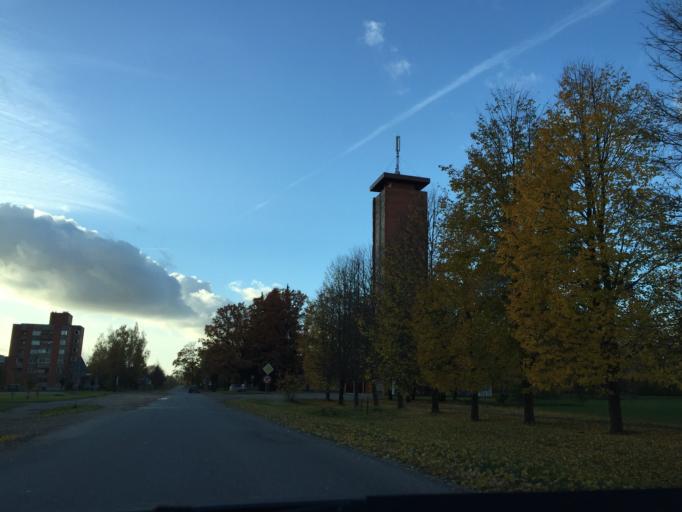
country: LV
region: Ogre
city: Jumprava
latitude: 56.7674
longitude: 25.0025
